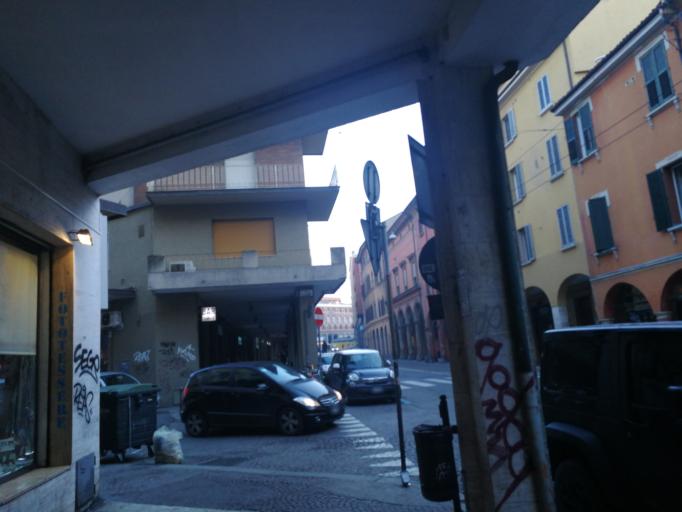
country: IT
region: Emilia-Romagna
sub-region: Provincia di Bologna
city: Bologna
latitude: 44.4982
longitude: 11.3359
